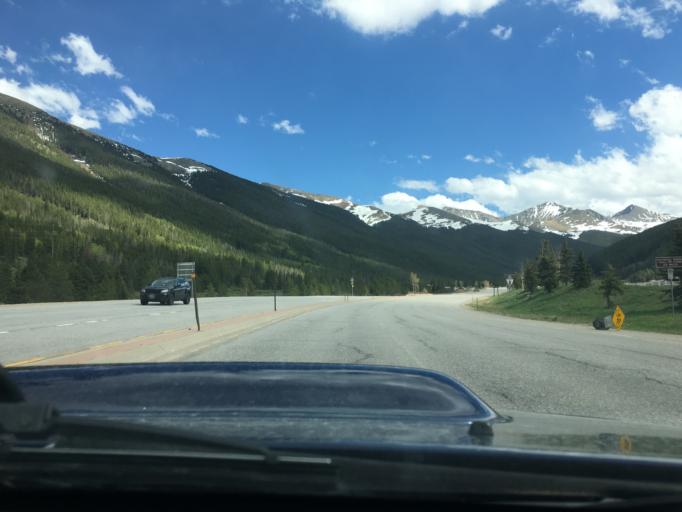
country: US
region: Colorado
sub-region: Summit County
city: Frisco
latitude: 39.5040
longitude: -106.1414
